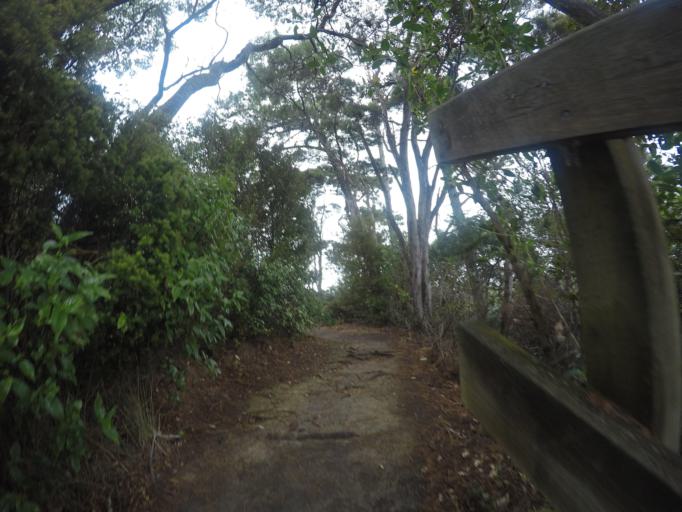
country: NZ
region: Auckland
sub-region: Auckland
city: North Shore
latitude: -36.7803
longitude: 174.6988
